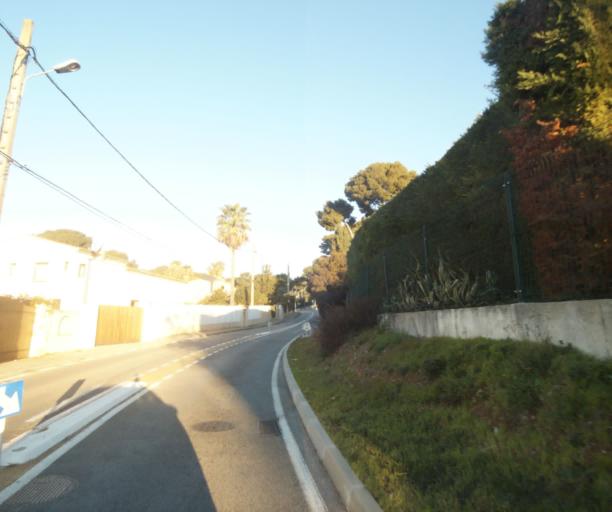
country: FR
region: Provence-Alpes-Cote d'Azur
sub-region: Departement des Alpes-Maritimes
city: Vallauris
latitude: 43.5797
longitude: 7.0838
